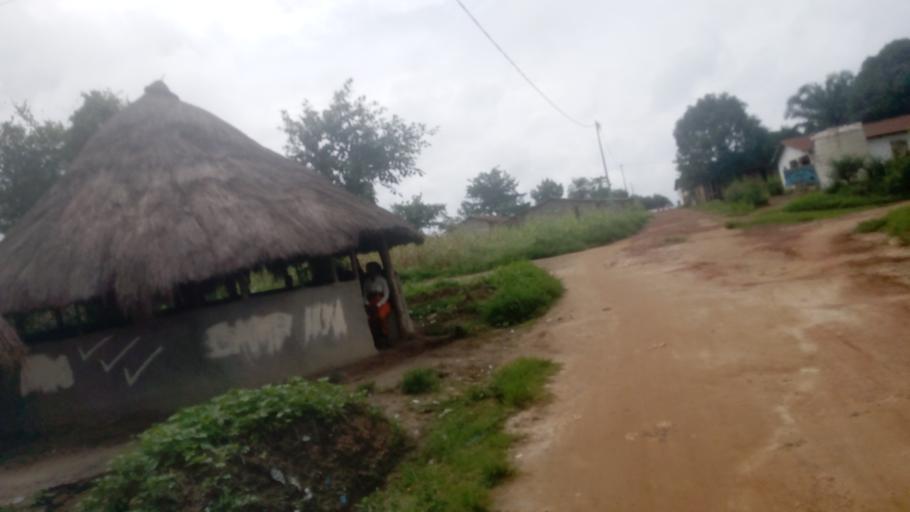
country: SL
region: Northern Province
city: Lunsar
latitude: 8.6929
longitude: -12.5377
